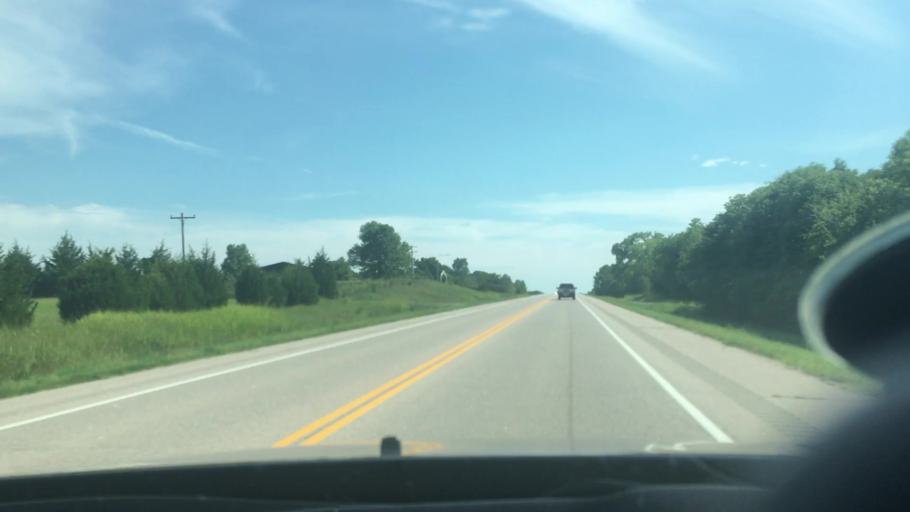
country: US
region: Oklahoma
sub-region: Seminole County
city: Konawa
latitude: 35.0189
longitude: -96.6784
